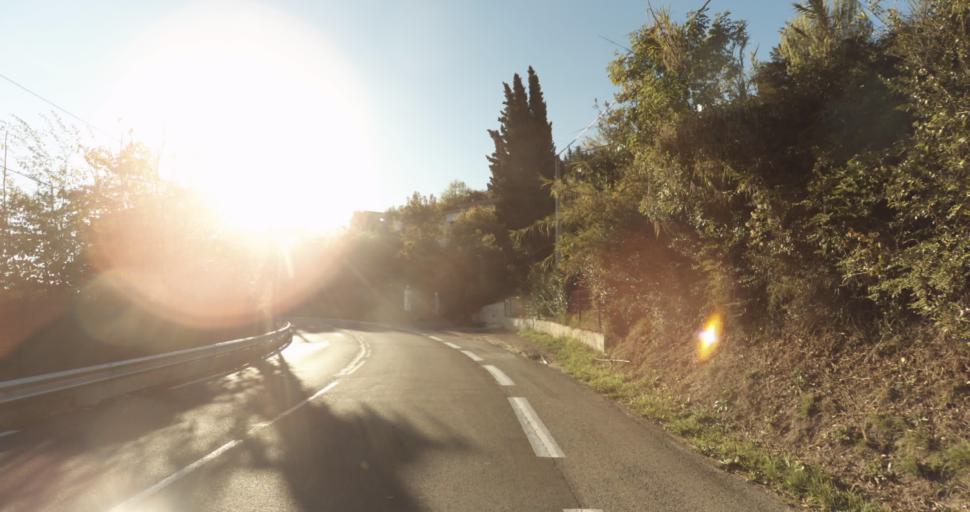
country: FR
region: Provence-Alpes-Cote d'Azur
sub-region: Departement des Alpes-Maritimes
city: Saint-Jeannet
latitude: 43.7390
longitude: 7.1313
